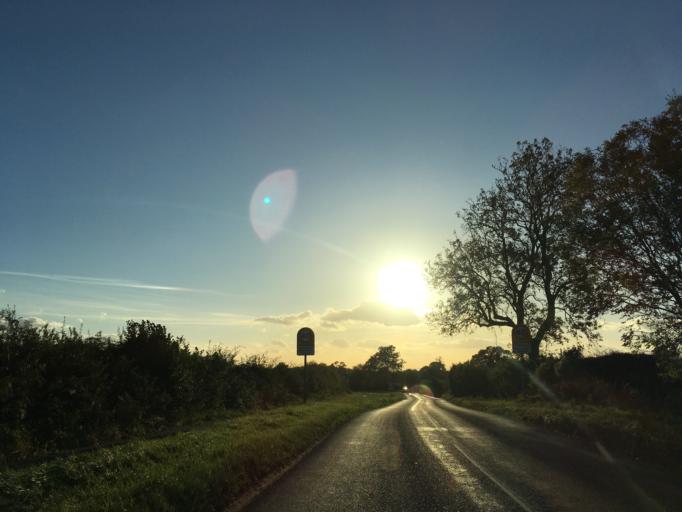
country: GB
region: England
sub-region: South Gloucestershire
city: Alveston
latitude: 51.5867
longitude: -2.5506
